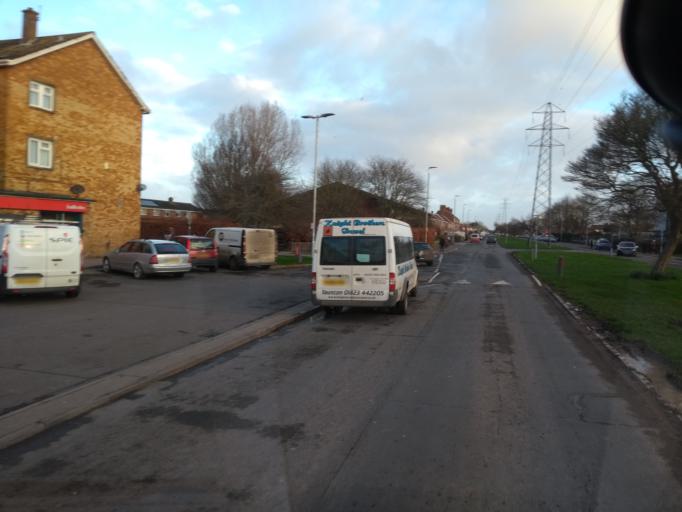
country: GB
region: England
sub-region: Somerset
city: Bridgwater
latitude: 51.1314
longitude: -2.9826
